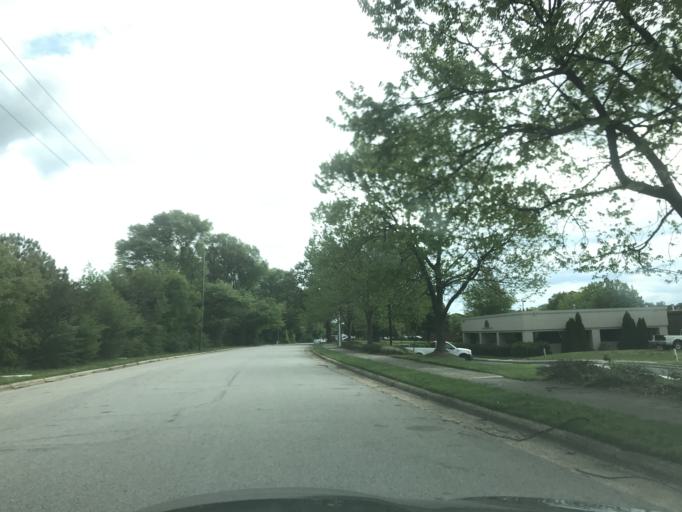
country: US
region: North Carolina
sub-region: Wake County
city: West Raleigh
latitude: 35.7947
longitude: -78.7029
